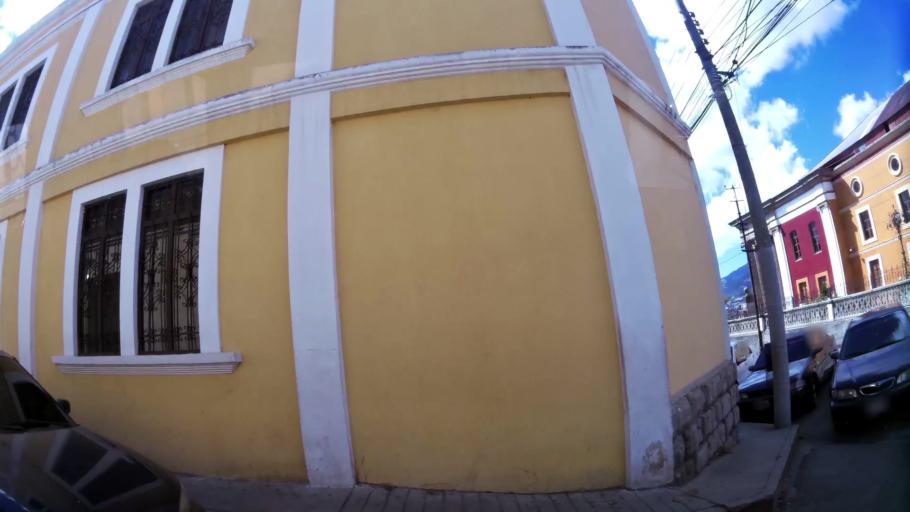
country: GT
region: Quetzaltenango
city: Quetzaltenango
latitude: 14.8380
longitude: -91.5185
